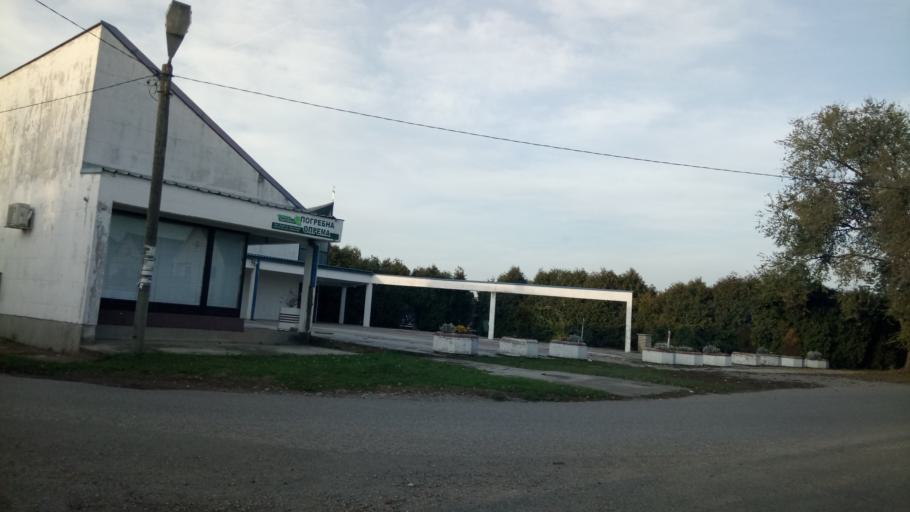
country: RS
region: Autonomna Pokrajina Vojvodina
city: Nova Pazova
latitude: 44.9385
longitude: 20.2195
